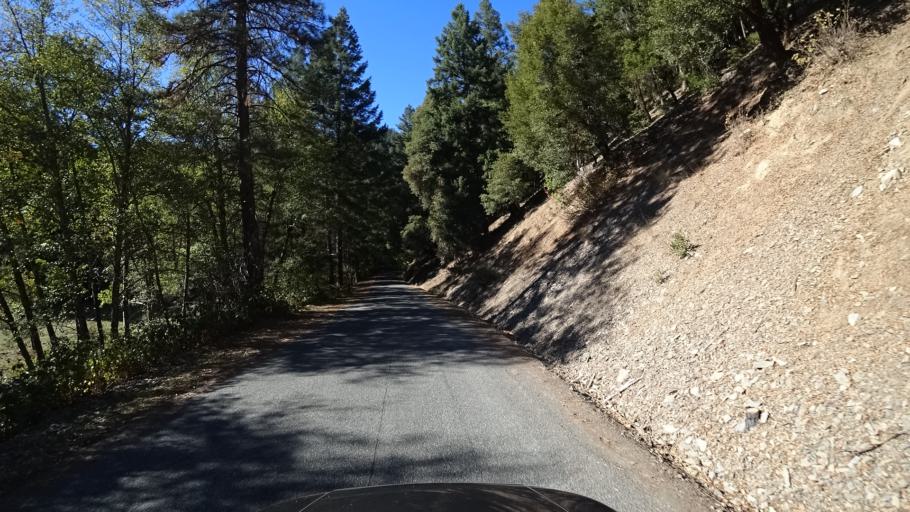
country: US
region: California
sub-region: Siskiyou County
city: Happy Camp
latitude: 41.3087
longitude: -123.1680
